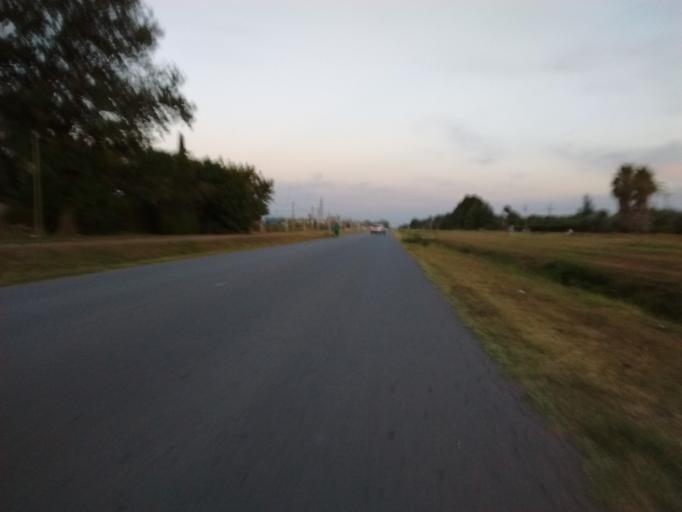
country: AR
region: Santa Fe
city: Roldan
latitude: -32.9025
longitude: -60.8900
